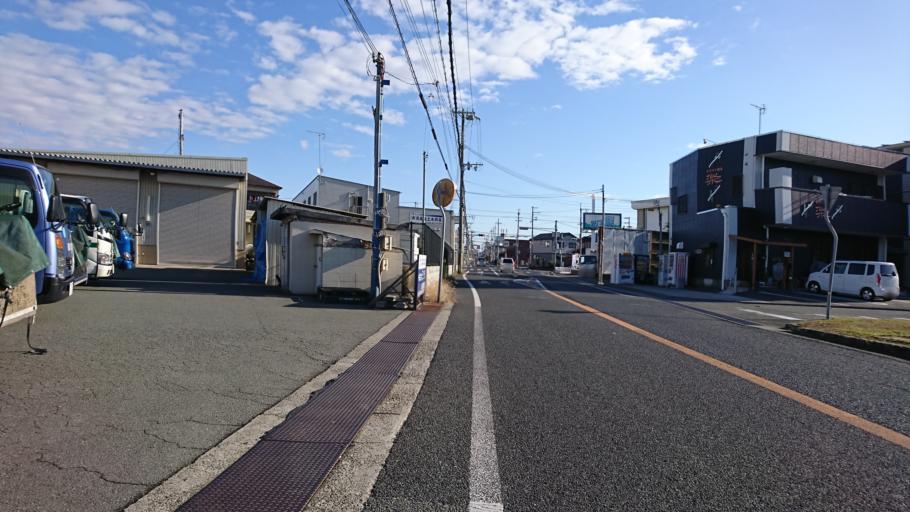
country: JP
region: Hyogo
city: Kakogawacho-honmachi
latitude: 34.7510
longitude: 134.8452
